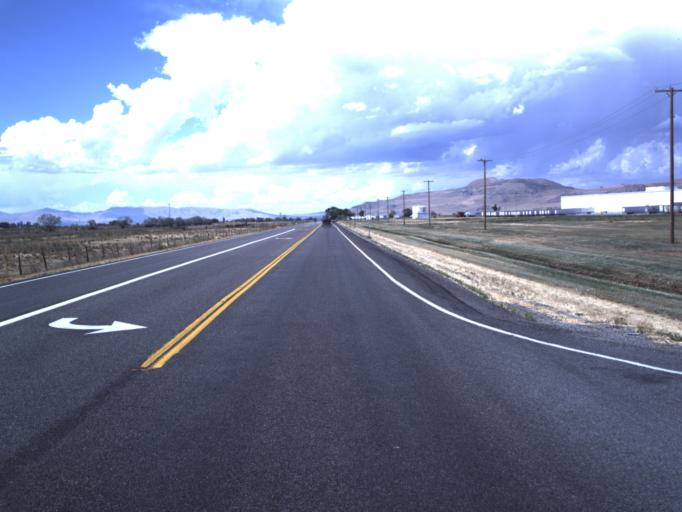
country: US
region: Utah
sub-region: Box Elder County
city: Honeyville
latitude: 41.5574
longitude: -112.1395
